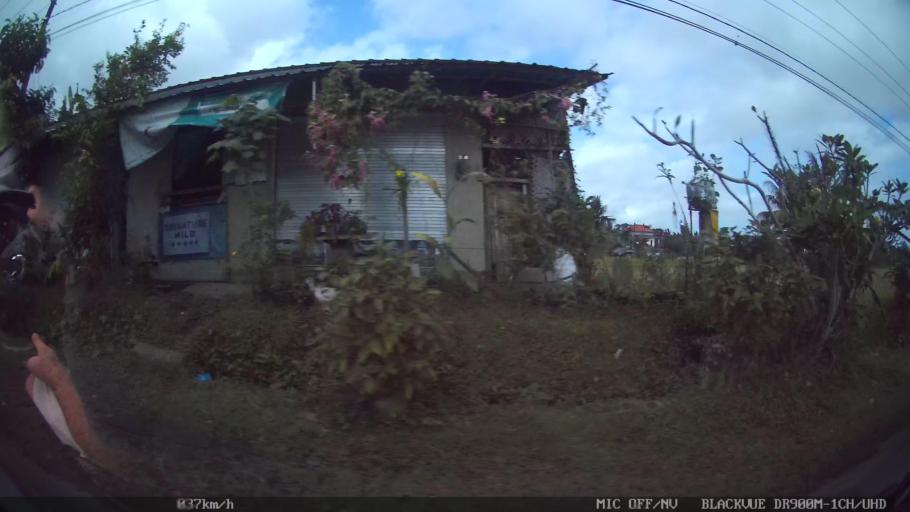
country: ID
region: Bali
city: Banjar Pesalakan
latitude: -8.4875
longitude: 115.3046
